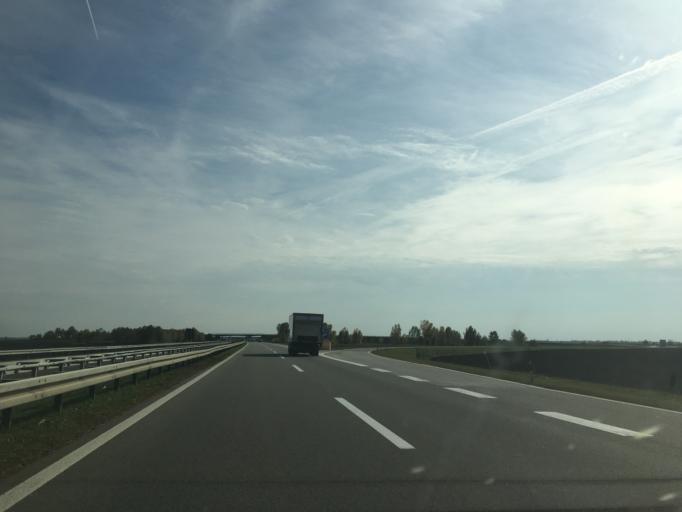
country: RS
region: Autonomna Pokrajina Vojvodina
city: Nova Pazova
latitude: 44.9917
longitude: 20.2108
